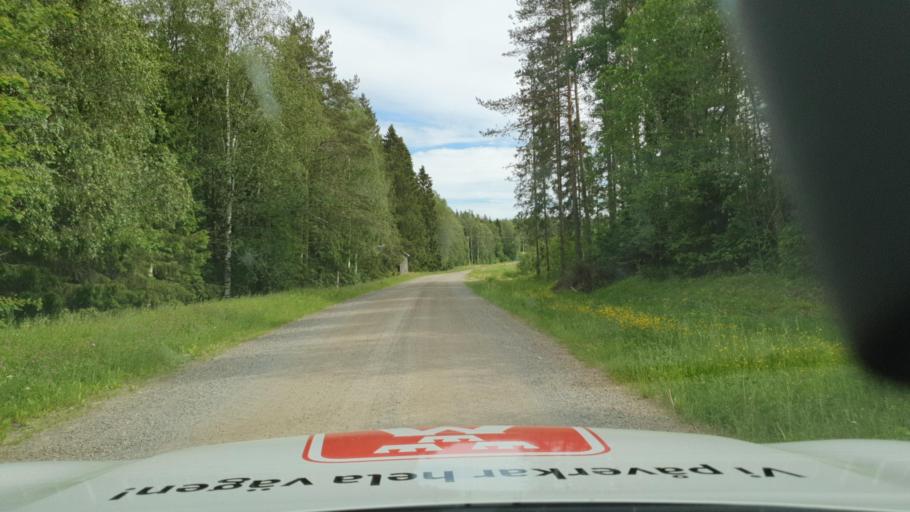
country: SE
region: Vaesterbotten
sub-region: Robertsfors Kommun
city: Robertsfors
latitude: 64.3873
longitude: 21.0366
